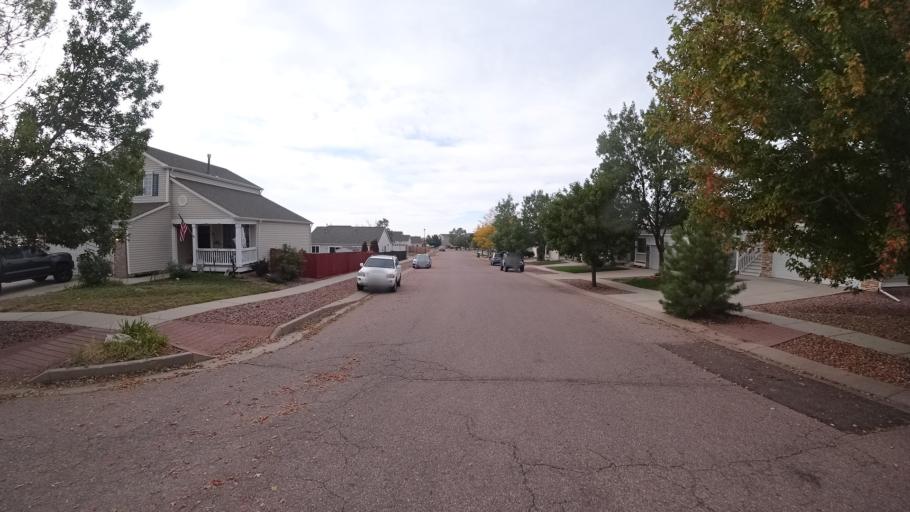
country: US
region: Colorado
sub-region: El Paso County
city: Cimarron Hills
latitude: 38.9173
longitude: -104.7057
